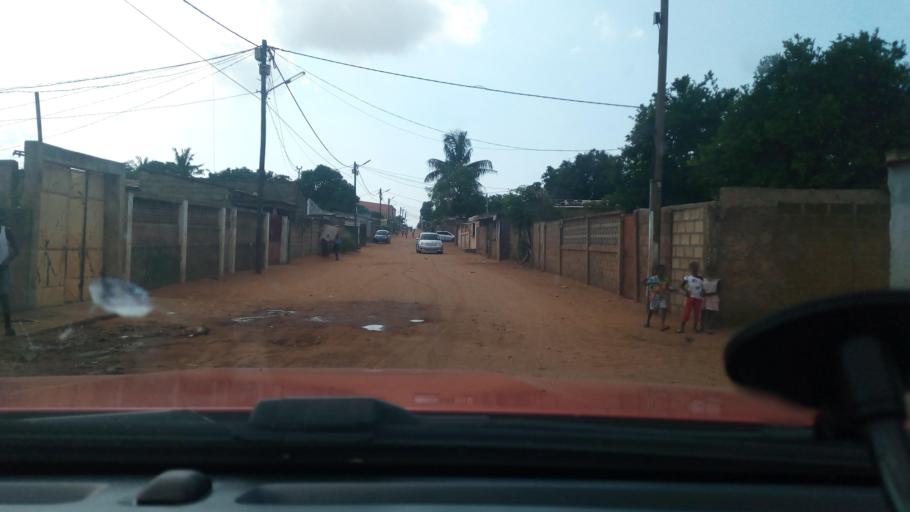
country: MZ
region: Maputo City
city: Maputo
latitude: -25.9224
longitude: 32.5910
